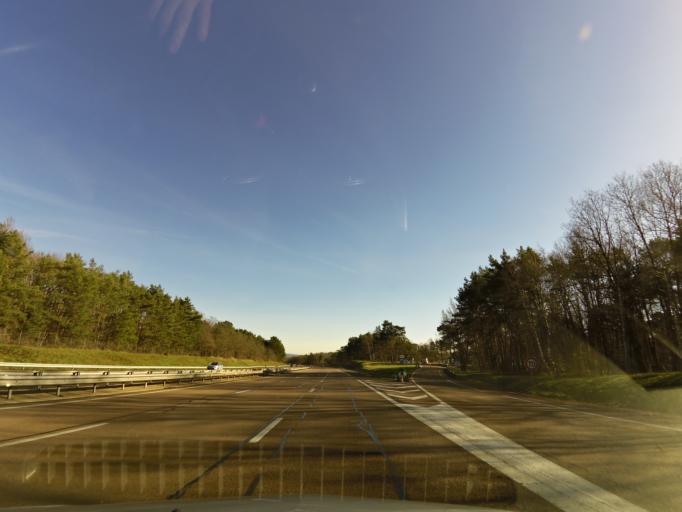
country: FR
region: Bourgogne
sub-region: Departement de l'Yonne
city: Appoigny
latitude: 47.8666
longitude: 3.4944
